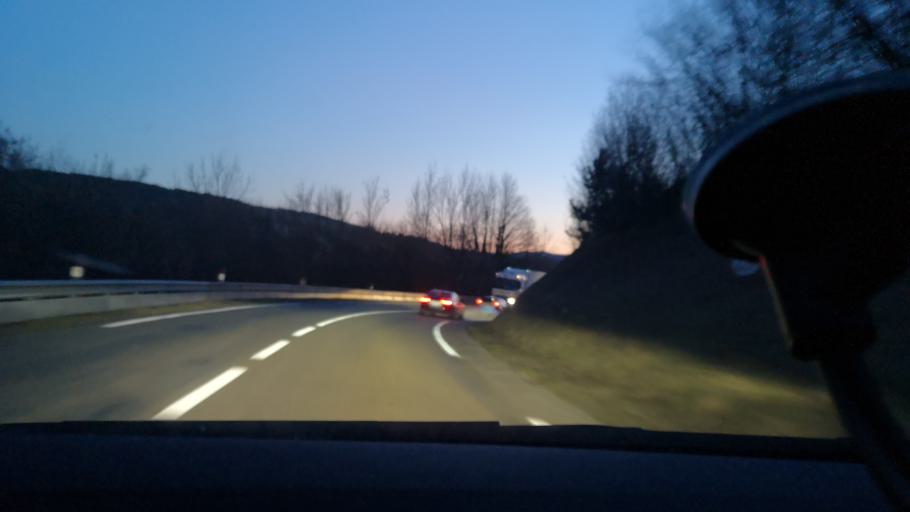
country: FR
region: Franche-Comte
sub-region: Departement du Jura
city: Champagnole
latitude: 46.7535
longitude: 5.9335
